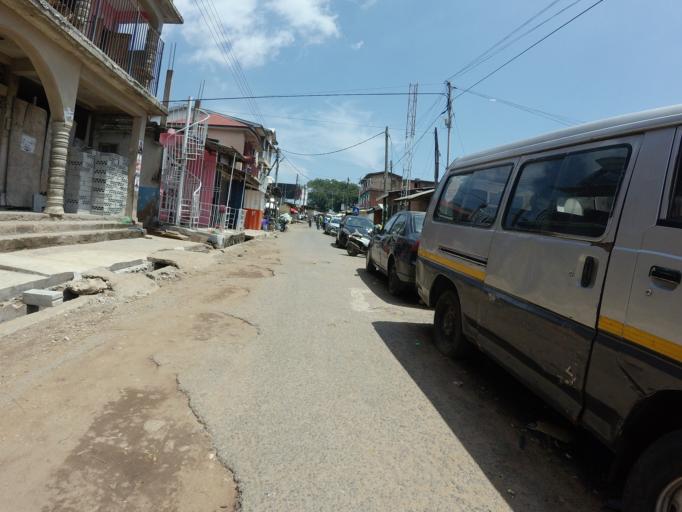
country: GH
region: Greater Accra
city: Accra
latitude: 5.5818
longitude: -0.1998
